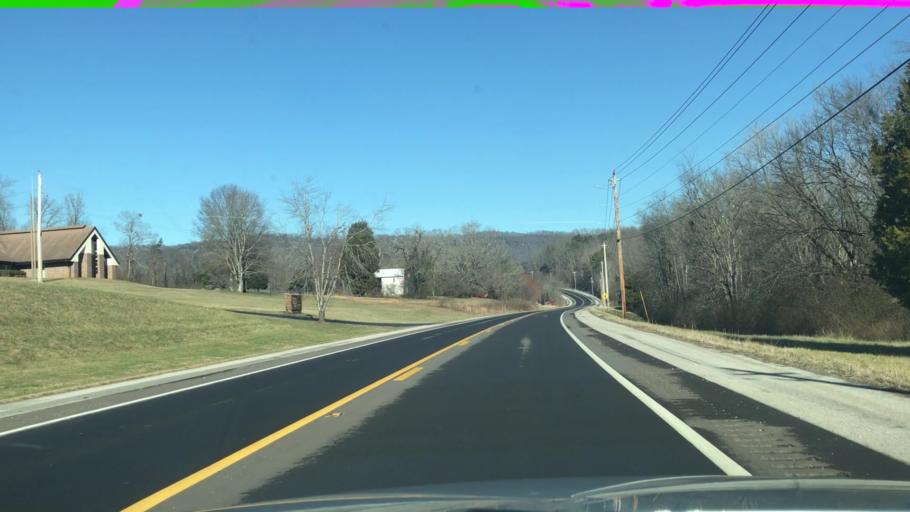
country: US
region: Tennessee
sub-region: Roane County
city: Midtown
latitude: 35.8849
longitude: -84.6175
